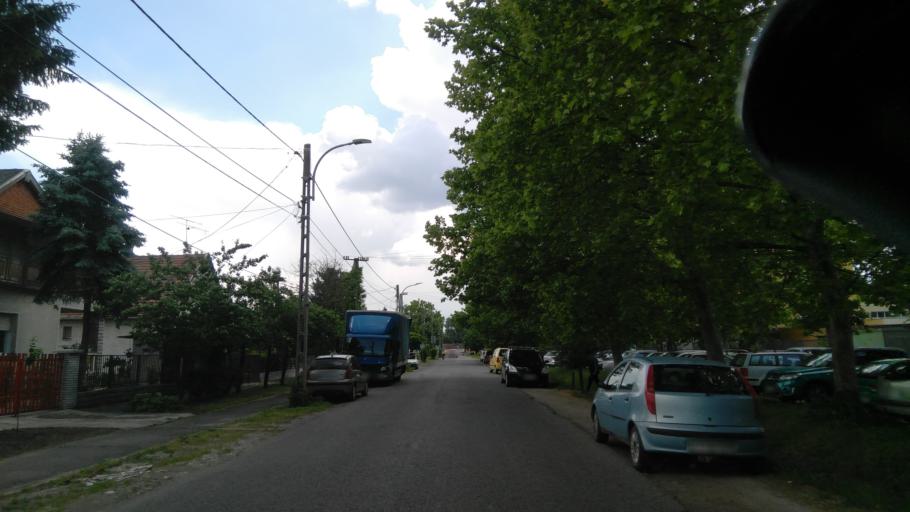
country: HU
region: Bekes
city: Gyula
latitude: 46.6595
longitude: 21.2695
